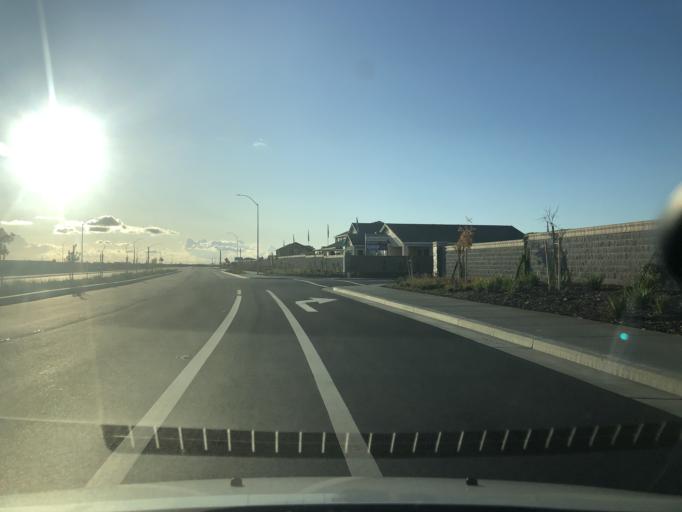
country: US
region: California
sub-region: Sacramento County
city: Antelope
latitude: 38.7613
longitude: -121.3614
